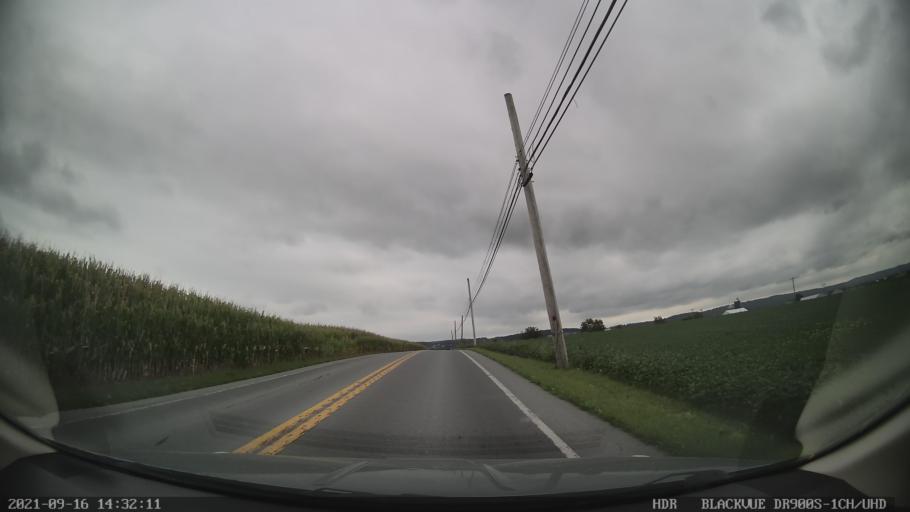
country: US
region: Pennsylvania
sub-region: Berks County
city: Kutztown
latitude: 40.4998
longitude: -75.7661
